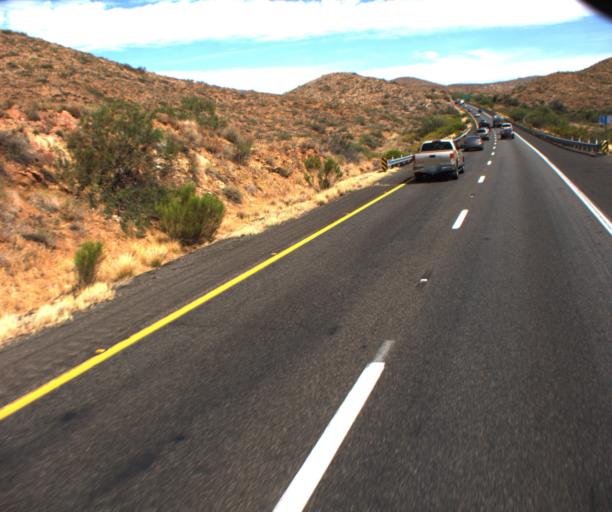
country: US
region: Arizona
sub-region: Yavapai County
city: Cordes Lakes
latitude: 34.2637
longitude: -112.1110
